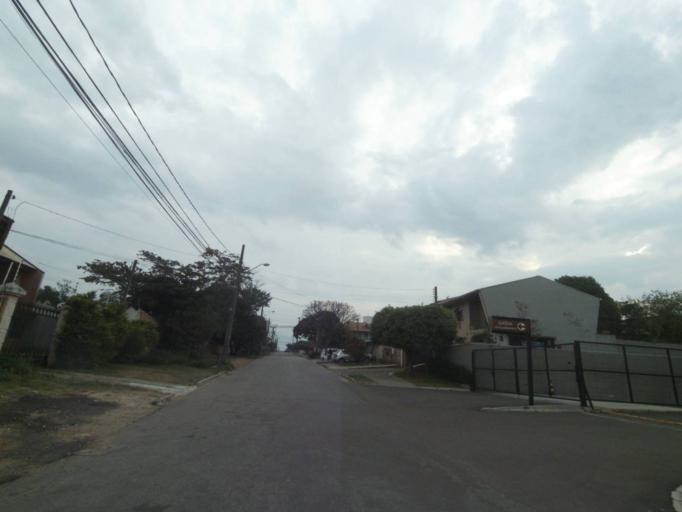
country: BR
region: Parana
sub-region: Pinhais
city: Pinhais
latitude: -25.4691
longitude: -49.2326
